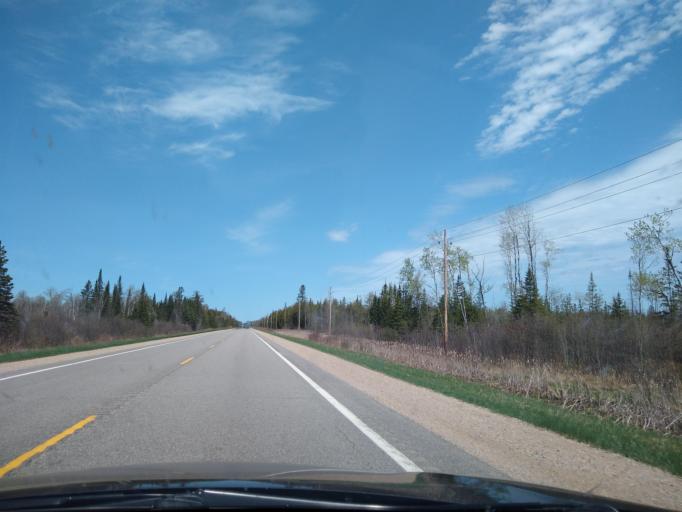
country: US
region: Michigan
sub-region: Delta County
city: Gladstone
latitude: 46.1021
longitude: -86.9807
